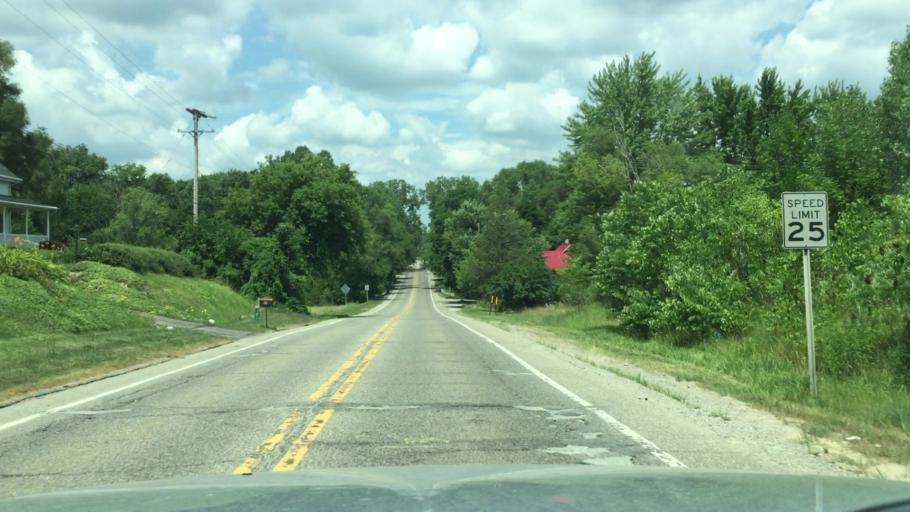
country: US
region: Michigan
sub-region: Genesee County
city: Flushing
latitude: 43.0644
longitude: -83.8638
